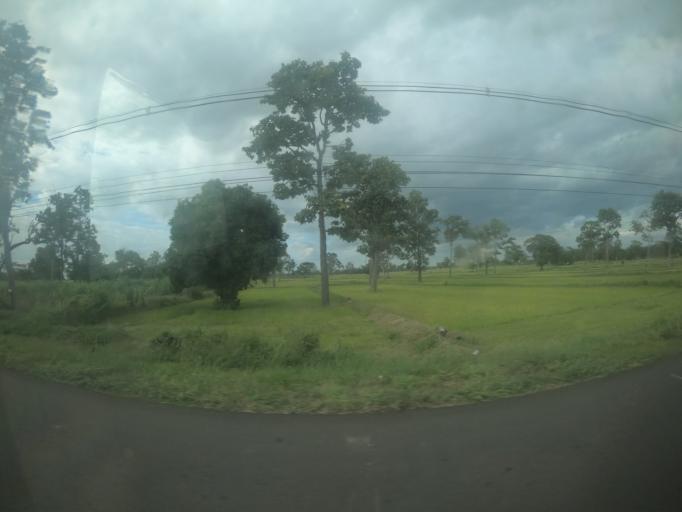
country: TH
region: Surin
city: Kap Choeng
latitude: 14.5409
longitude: 103.5200
